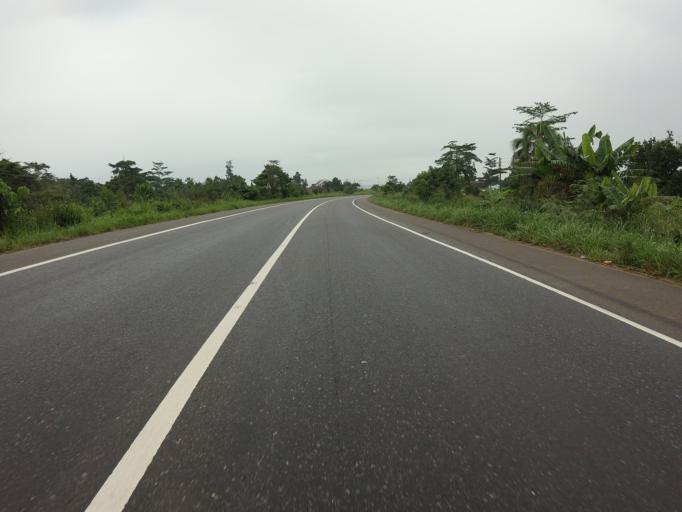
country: GH
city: Kibi
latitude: 6.1616
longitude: -0.4833
